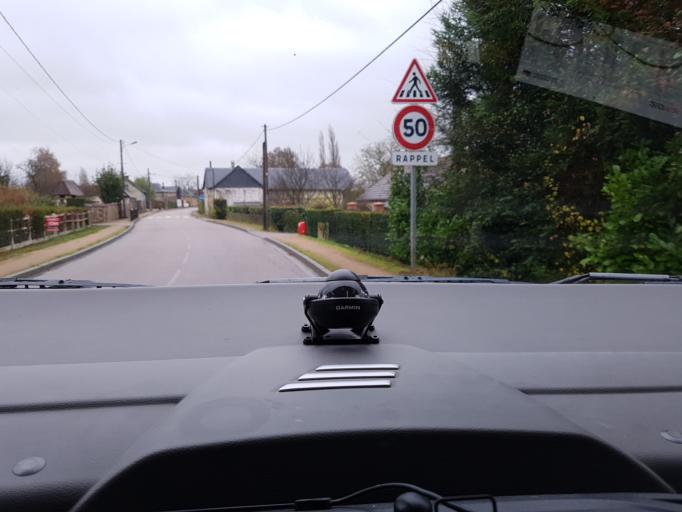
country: FR
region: Haute-Normandie
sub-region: Departement de l'Eure
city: Pont-Saint-Pierre
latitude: 49.3143
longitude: 1.3068
